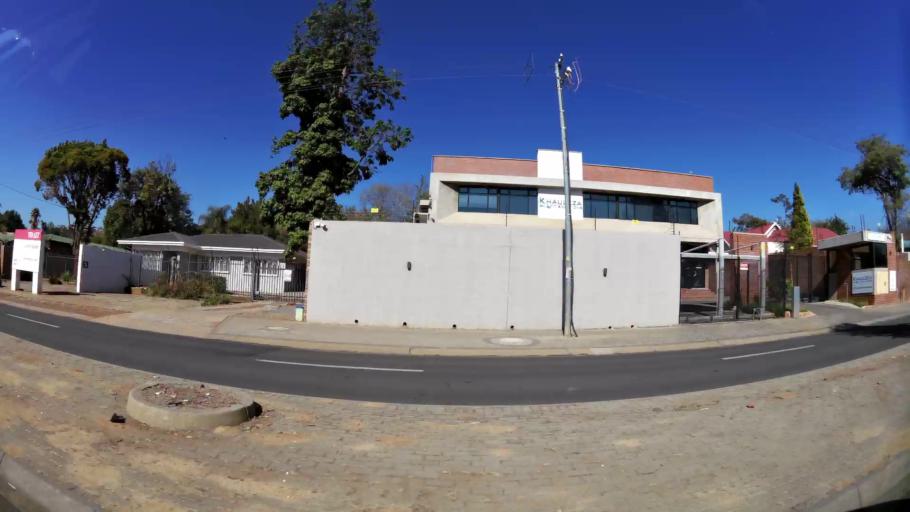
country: ZA
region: Gauteng
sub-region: City of Tshwane Metropolitan Municipality
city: Pretoria
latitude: -25.7724
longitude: 28.2178
